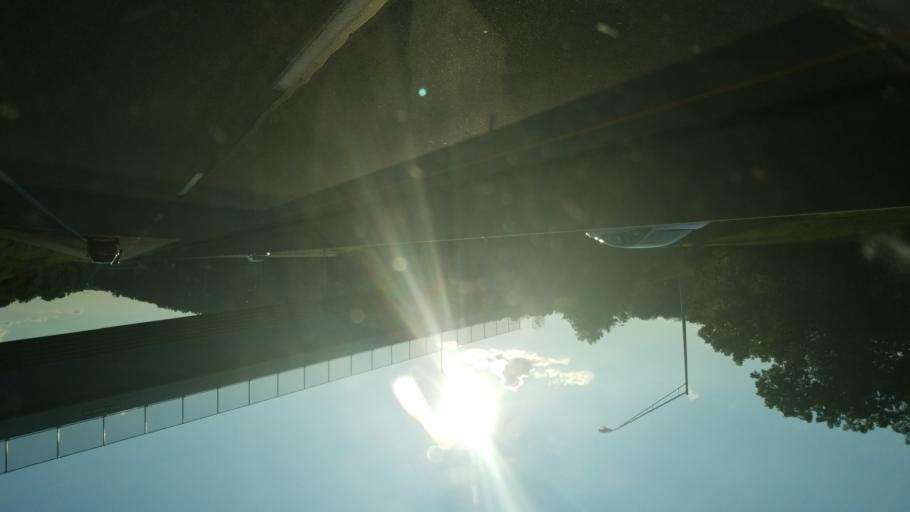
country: US
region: Pennsylvania
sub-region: Beaver County
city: Big Beaver
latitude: 40.8372
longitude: -80.3785
